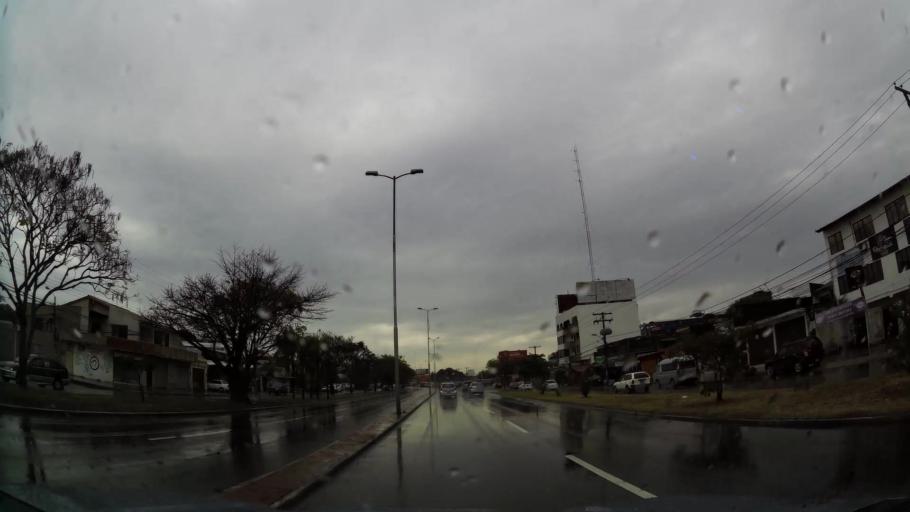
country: BO
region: Santa Cruz
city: Santa Cruz de la Sierra
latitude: -17.7896
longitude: -63.1650
